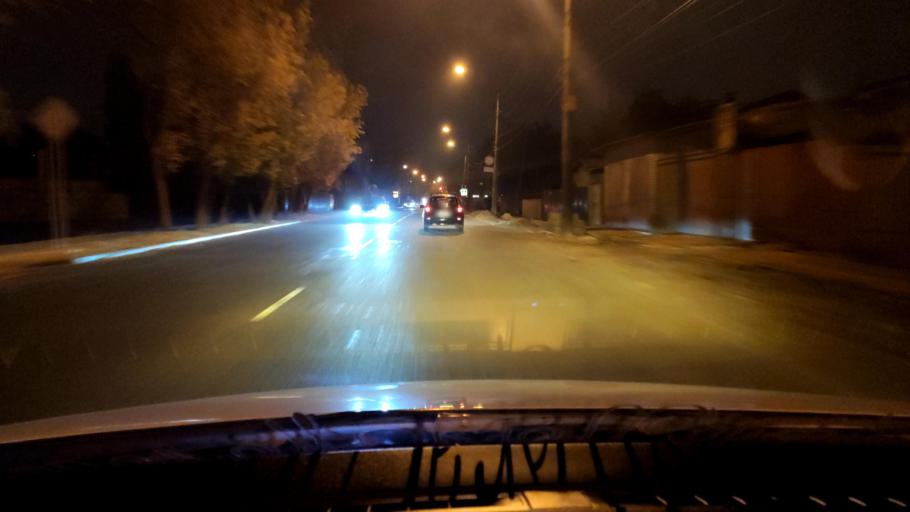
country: RU
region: Voronezj
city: Voronezh
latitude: 51.6862
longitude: 39.2114
